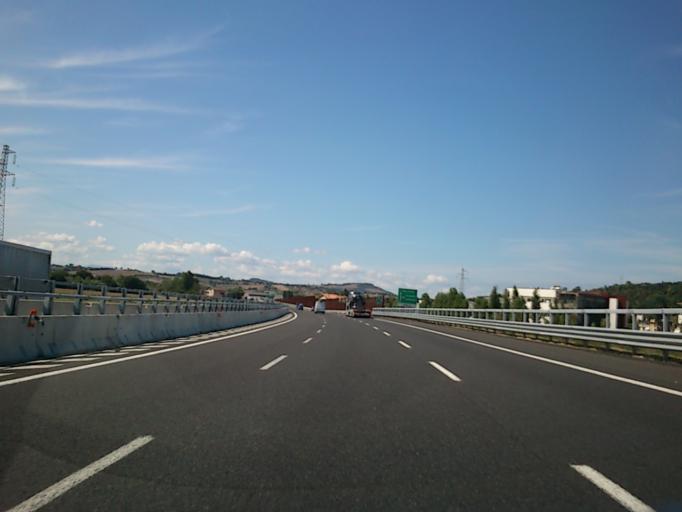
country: IT
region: The Marches
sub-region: Provincia di Pesaro e Urbino
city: Pesaro
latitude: 43.8995
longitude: 12.8650
